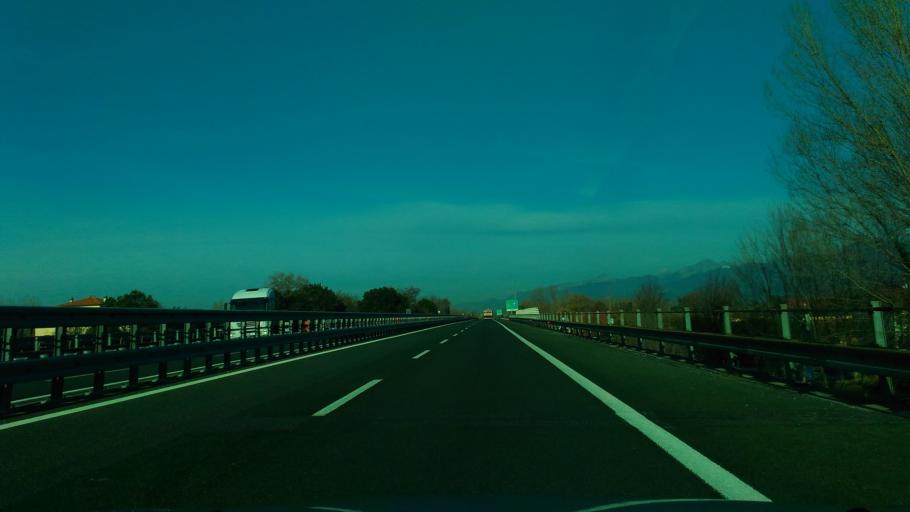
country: IT
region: Tuscany
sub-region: Provincia di Lucca
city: Torre del Lago Puccini
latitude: 43.8301
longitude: 10.3007
